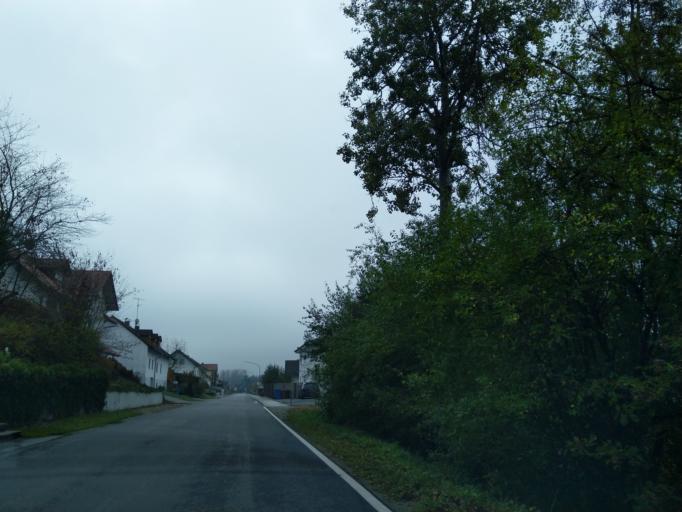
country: DE
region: Bavaria
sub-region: Lower Bavaria
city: Schollnach
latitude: 48.7613
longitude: 13.1796
